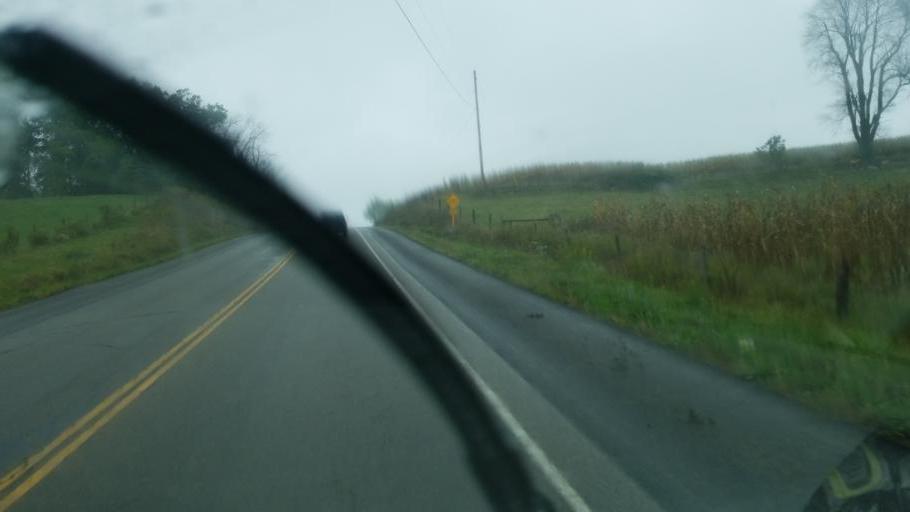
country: US
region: Ohio
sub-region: Holmes County
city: Millersburg
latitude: 40.5846
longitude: -81.7809
